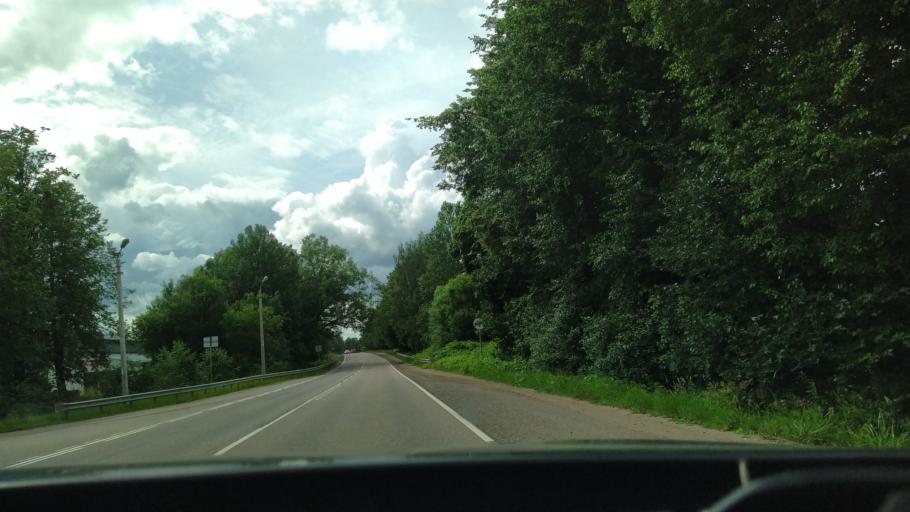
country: RU
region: Leningrad
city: Otradnoye
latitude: 59.7987
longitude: 30.8227
